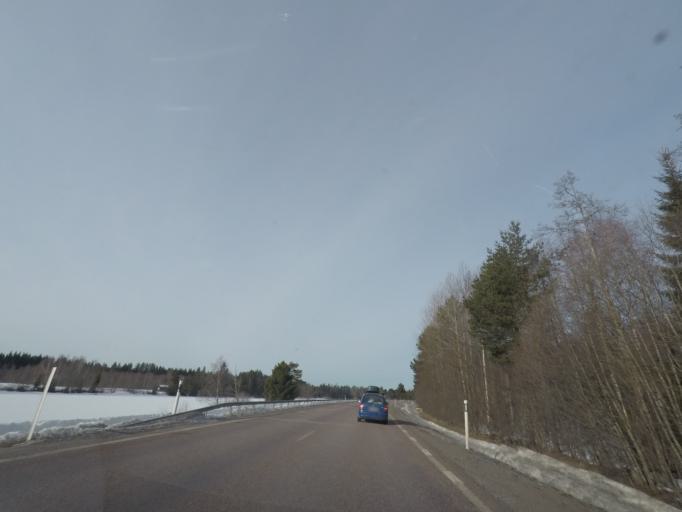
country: SE
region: Dalarna
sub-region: Gagnefs Kommun
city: Mockfjard
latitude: 60.4664
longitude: 14.6687
